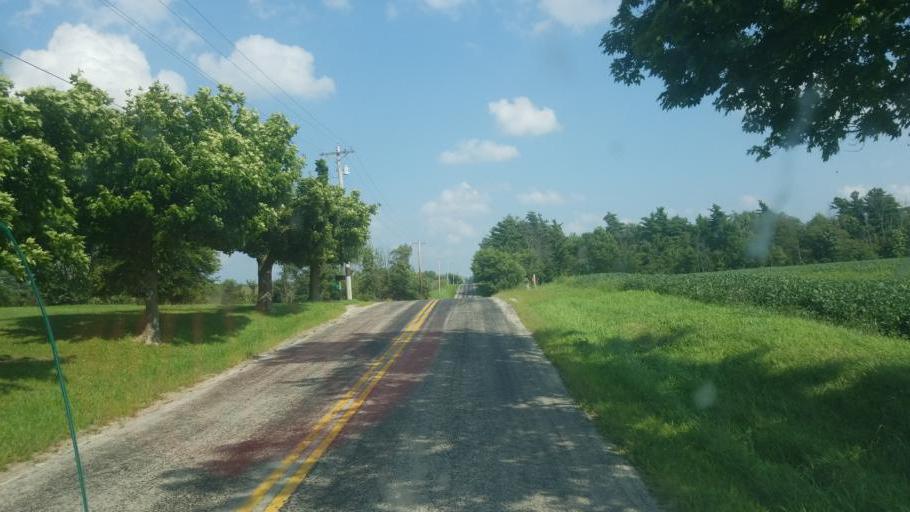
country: US
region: Ohio
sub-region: Lorain County
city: Wellington
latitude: 41.0576
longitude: -82.2660
